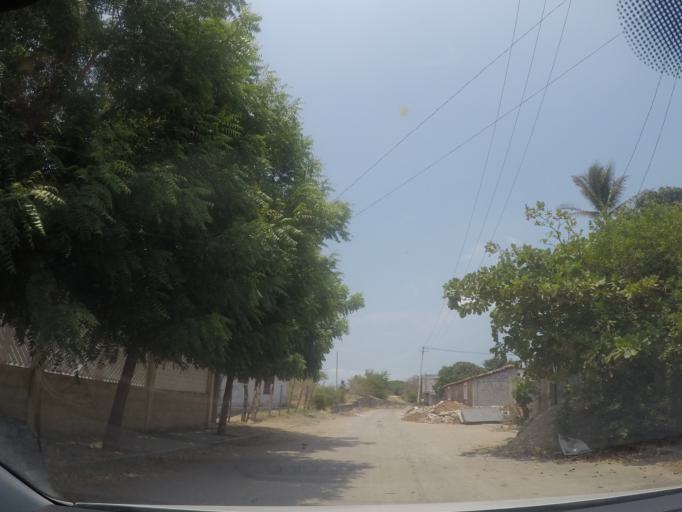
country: MX
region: Oaxaca
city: Asuncion Ixtaltepec
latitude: 16.5076
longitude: -95.0623
